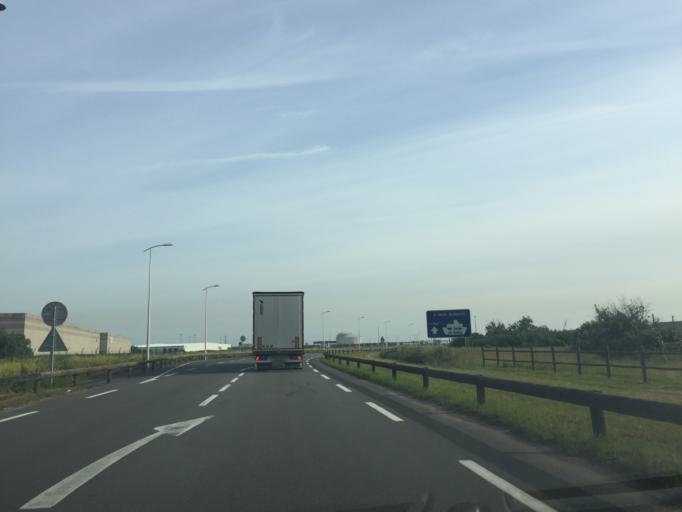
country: FR
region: Nord-Pas-de-Calais
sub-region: Departement du Nord
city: Loon-Plage
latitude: 51.0100
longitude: 2.1966
